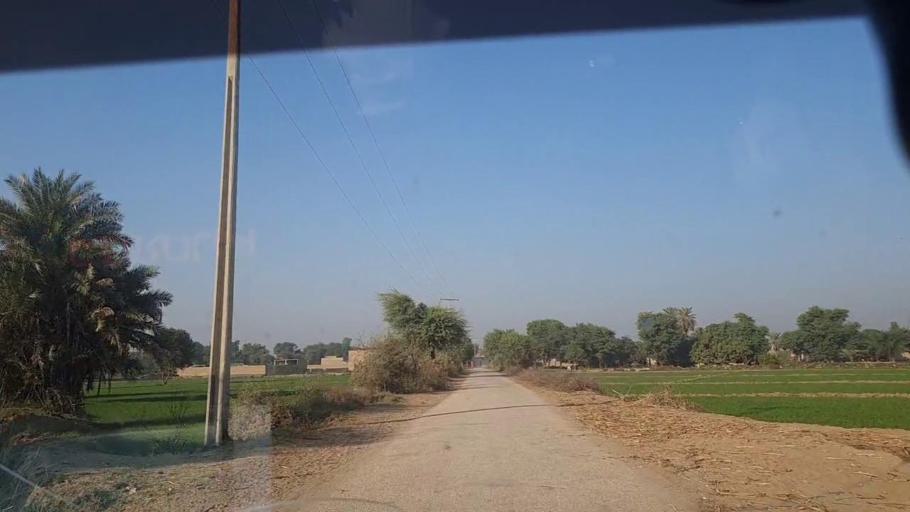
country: PK
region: Sindh
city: Sobhadero
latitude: 27.2528
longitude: 68.3505
